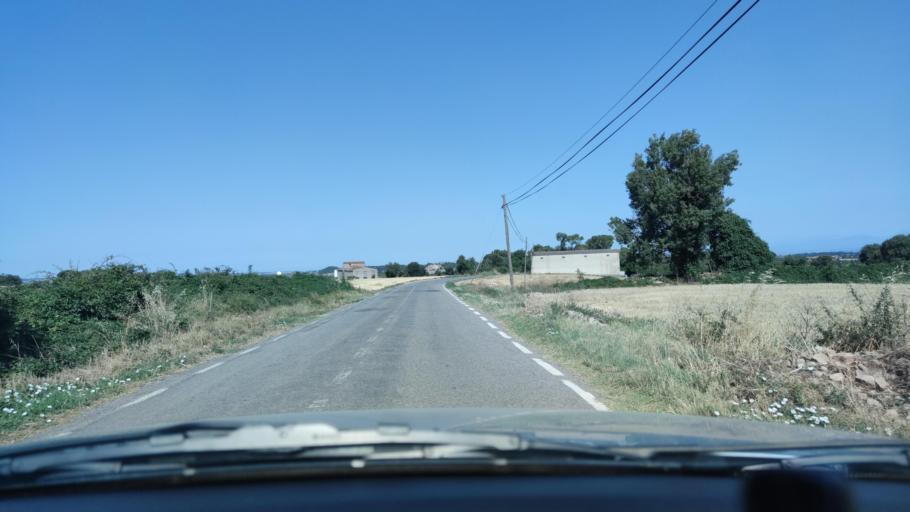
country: ES
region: Catalonia
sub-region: Provincia de Lleida
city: Sant Guim de Freixenet
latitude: 41.6442
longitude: 1.4115
